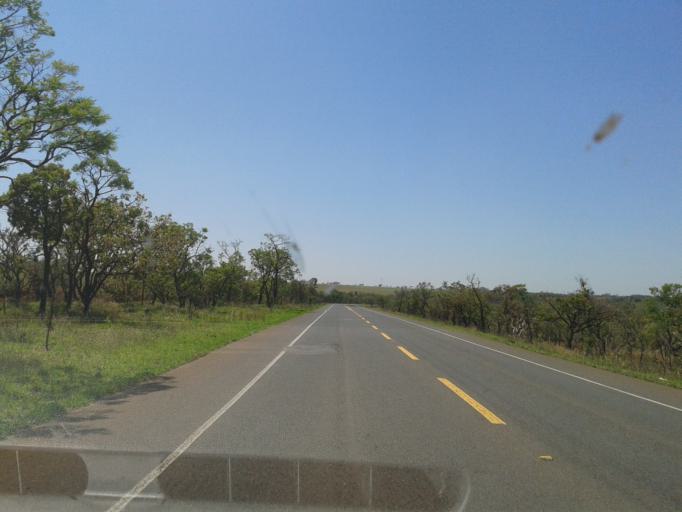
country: BR
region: Minas Gerais
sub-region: Patrocinio
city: Patrocinio
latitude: -19.2837
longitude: -47.4157
